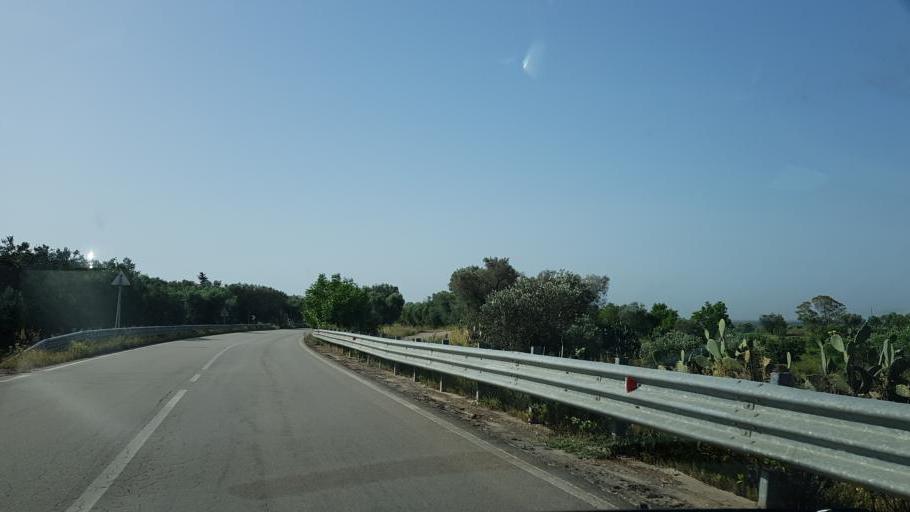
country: IT
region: Apulia
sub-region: Provincia di Brindisi
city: Mesagne
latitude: 40.4934
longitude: 17.8322
